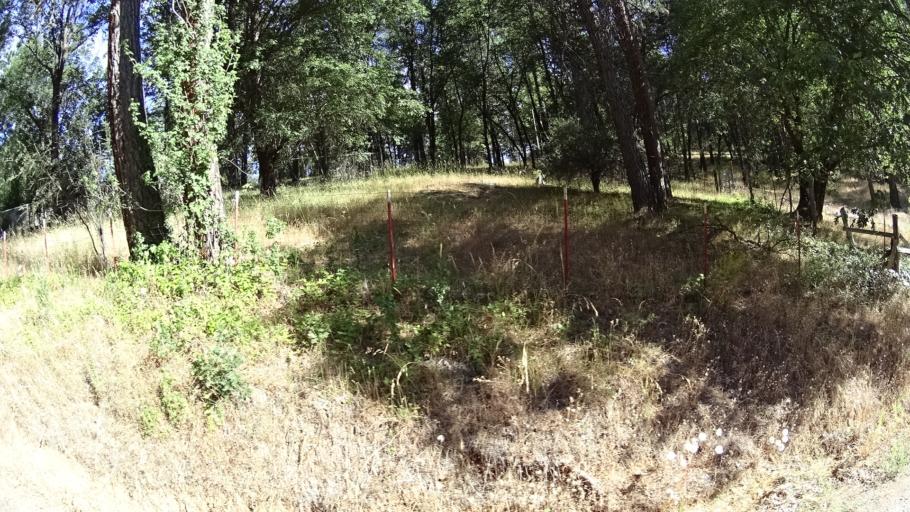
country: US
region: California
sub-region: Amador County
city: Pioneer
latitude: 38.3782
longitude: -120.5568
